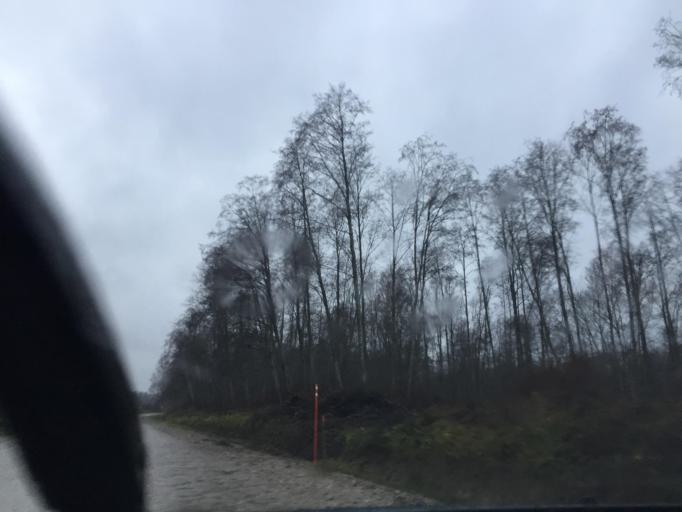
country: LV
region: Salacgrivas
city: Salacgriva
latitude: 57.7663
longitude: 24.4704
